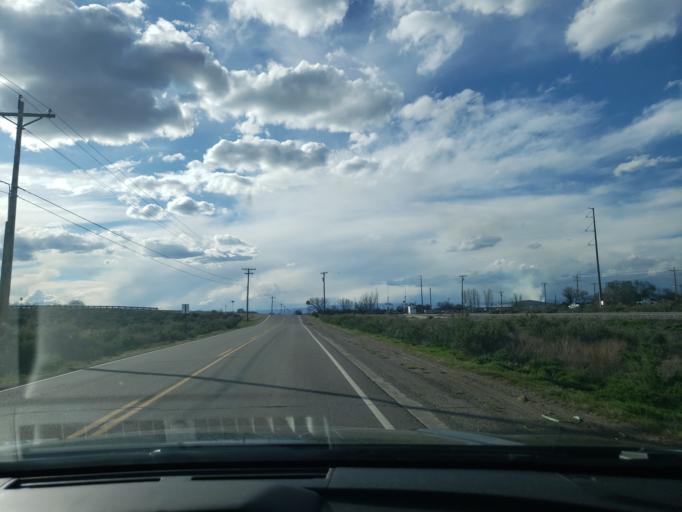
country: US
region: Colorado
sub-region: Mesa County
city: Fruita
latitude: 39.1280
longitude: -108.6813
